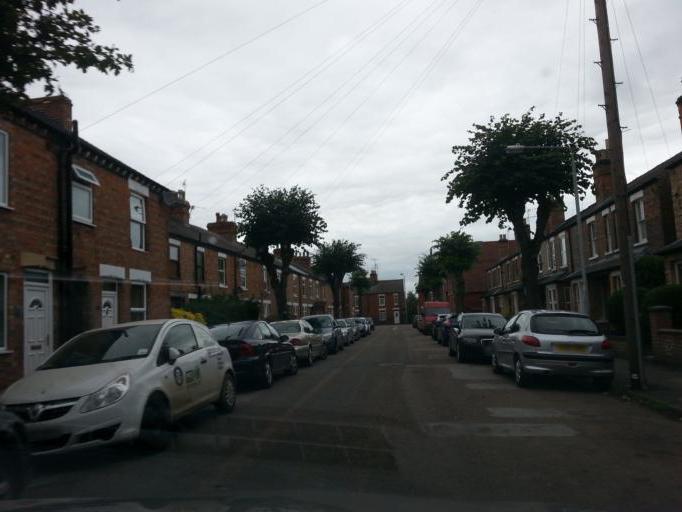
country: GB
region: England
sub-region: Nottinghamshire
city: Newark on Trent
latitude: 53.0719
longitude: -0.7977
